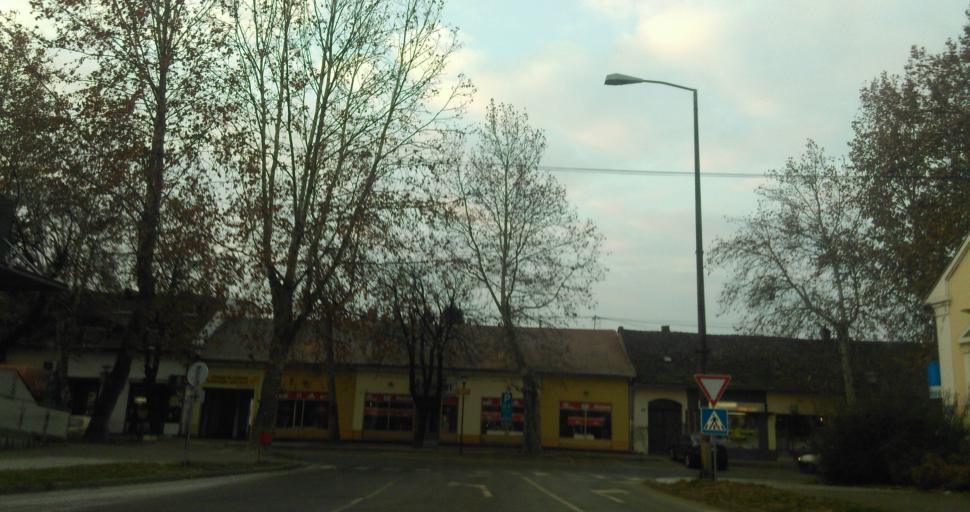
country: RS
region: Autonomna Pokrajina Vojvodina
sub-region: Juznobacki Okrug
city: Becej
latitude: 45.6153
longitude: 20.0466
